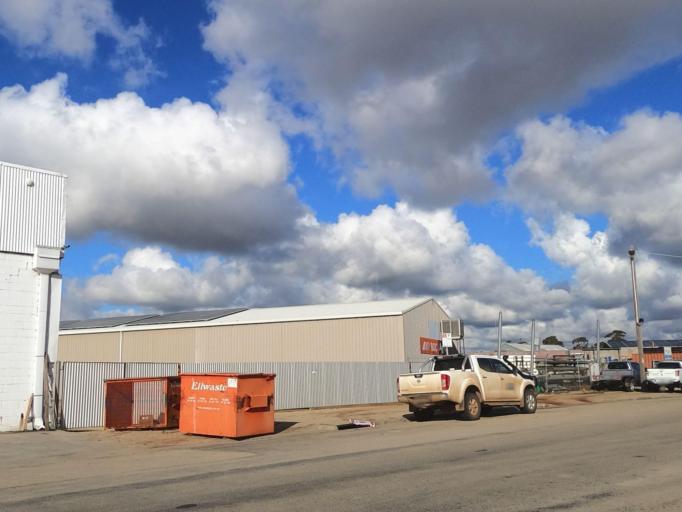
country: AU
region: Victoria
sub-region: Swan Hill
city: Swan Hill
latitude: -35.3293
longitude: 143.5530
